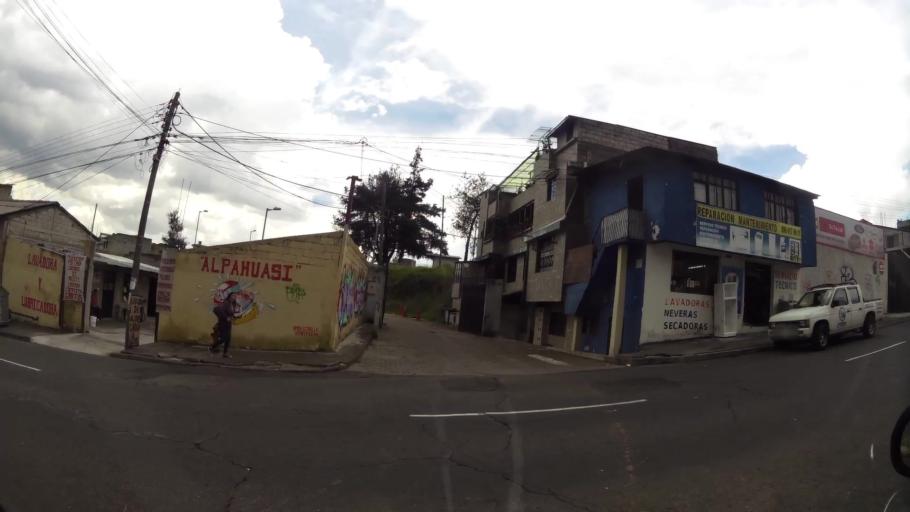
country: EC
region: Pichincha
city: Quito
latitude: -0.2439
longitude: -78.5116
